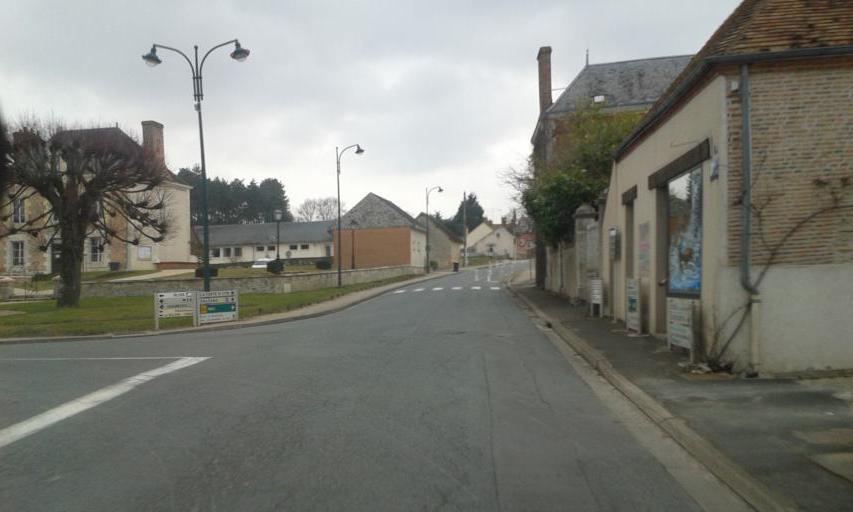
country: FR
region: Centre
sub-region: Departement du Loir-et-Cher
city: Dhuizon
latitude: 47.5890
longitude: 1.6585
